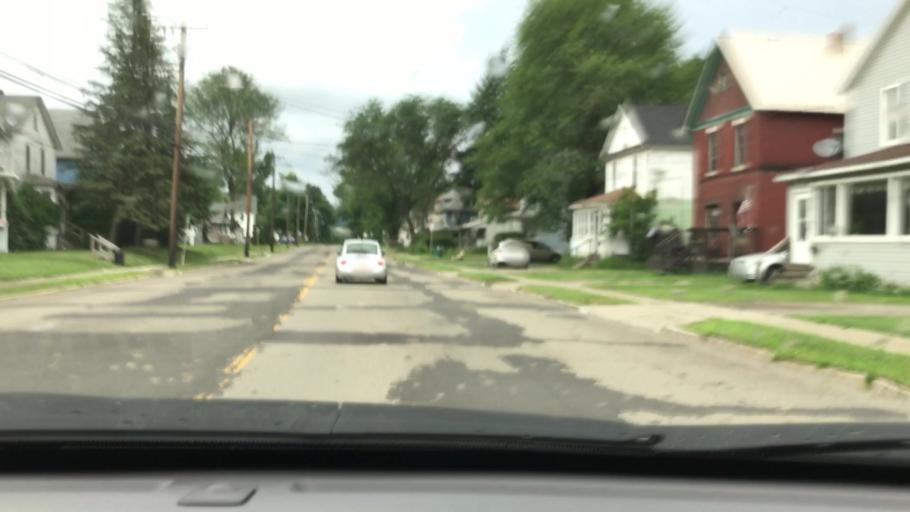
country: US
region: New York
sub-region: Cattaraugus County
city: Salamanca
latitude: 42.1668
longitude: -78.6941
